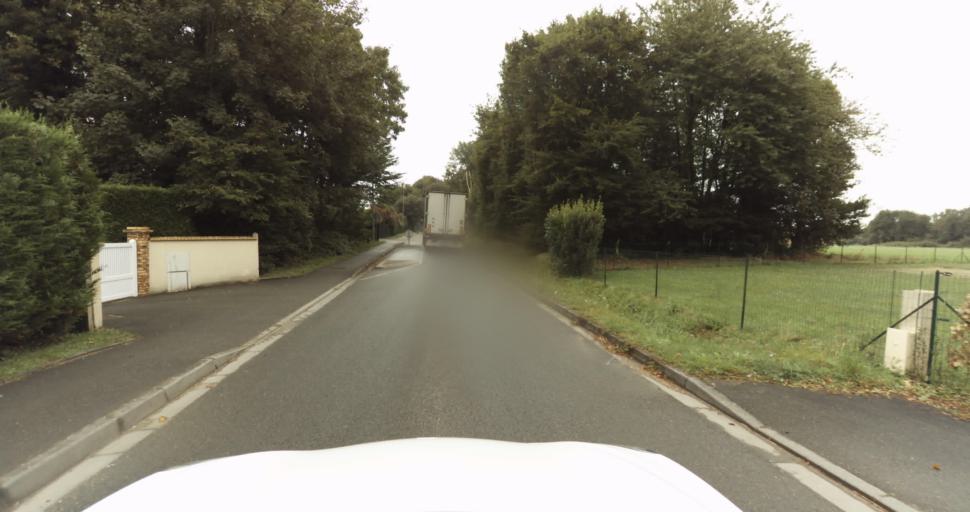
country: FR
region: Haute-Normandie
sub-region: Departement de l'Eure
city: Aviron
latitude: 49.0489
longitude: 1.1274
